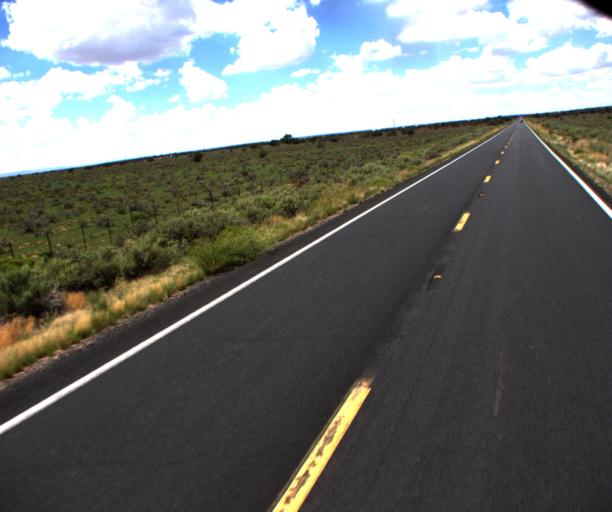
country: US
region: Arizona
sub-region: Coconino County
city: Williams
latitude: 35.6328
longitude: -112.1196
